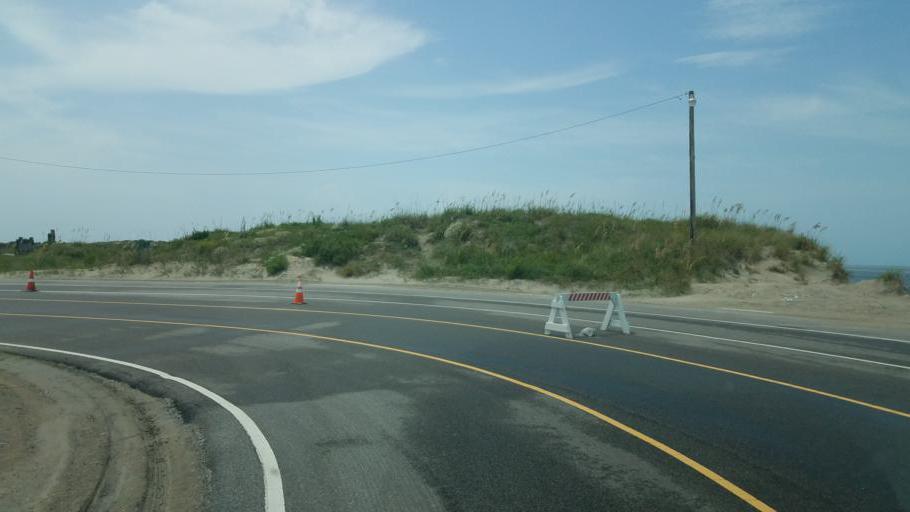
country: US
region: North Carolina
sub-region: Dare County
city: Buxton
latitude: 35.1907
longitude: -75.7793
